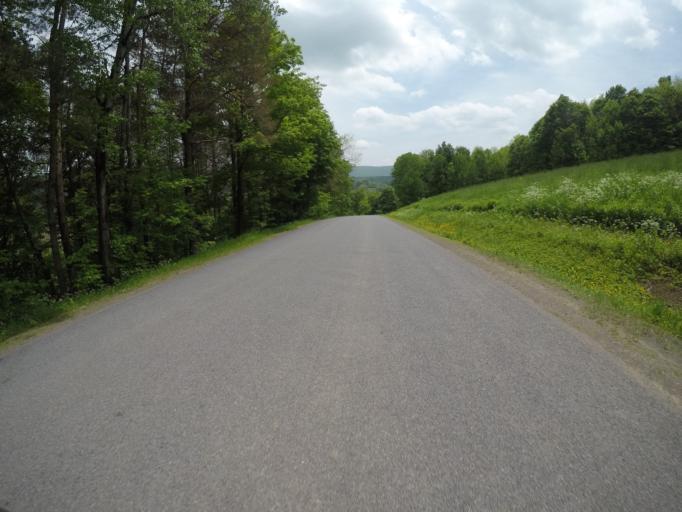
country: US
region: New York
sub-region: Delaware County
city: Stamford
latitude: 42.2370
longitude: -74.6980
